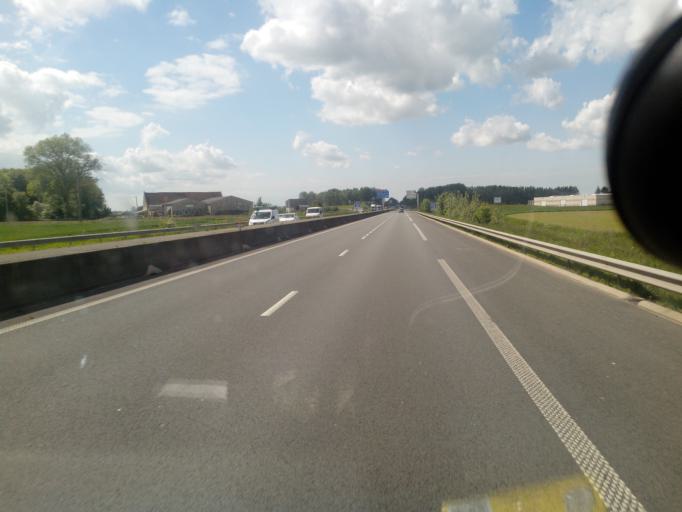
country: FR
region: Nord-Pas-de-Calais
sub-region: Departement du Nord
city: Quaedypre
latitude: 50.9460
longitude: 2.4411
